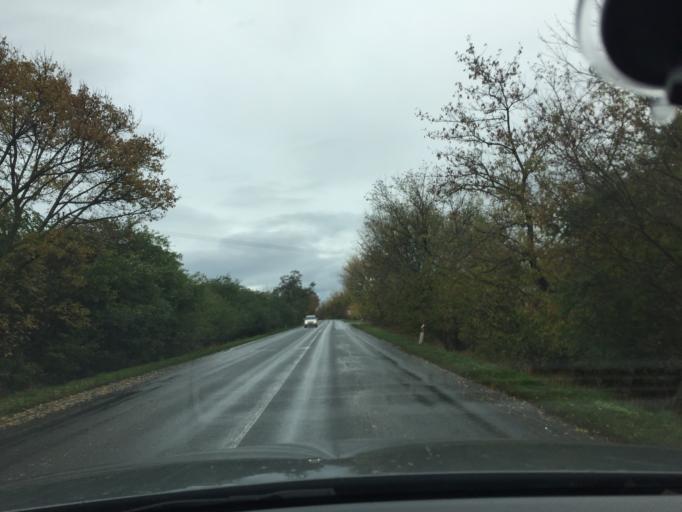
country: CZ
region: Central Bohemia
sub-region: Okres Melnik
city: Veltrusy
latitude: 50.3159
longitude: 14.3047
